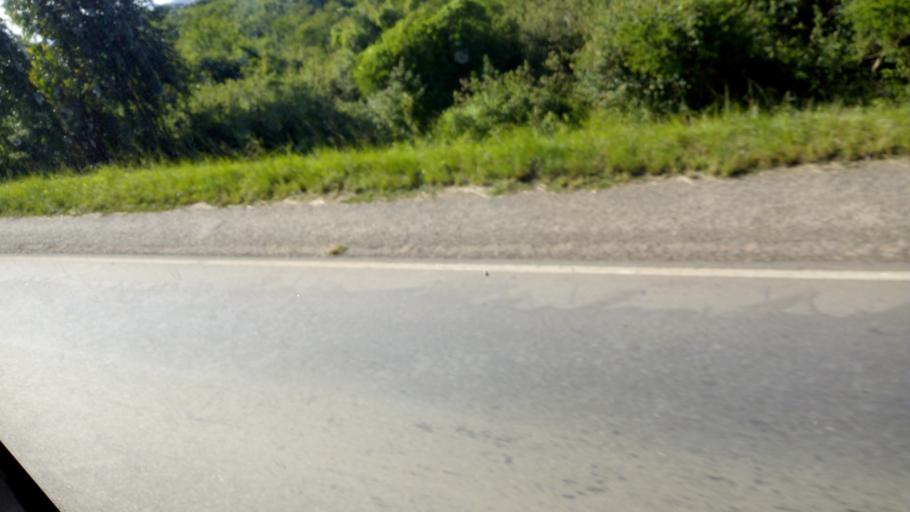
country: UG
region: Central Region
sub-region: Lyantonde District
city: Lyantonde
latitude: -0.4184
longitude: 31.1193
